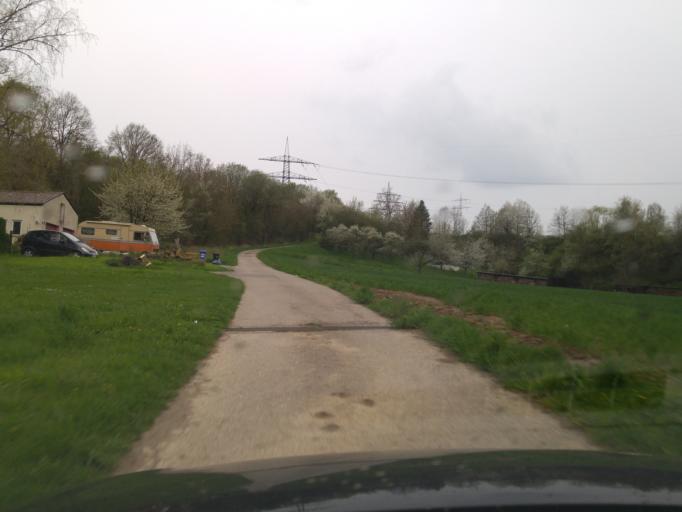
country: DE
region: Baden-Wuerttemberg
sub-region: Karlsruhe Region
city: Hassmersheim
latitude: 49.2973
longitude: 9.1293
